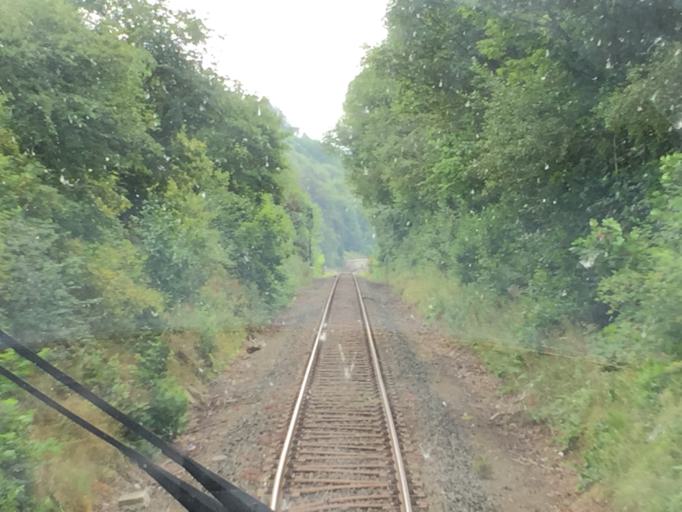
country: DE
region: Hesse
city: Willingen
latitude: 51.2915
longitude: 8.6122
